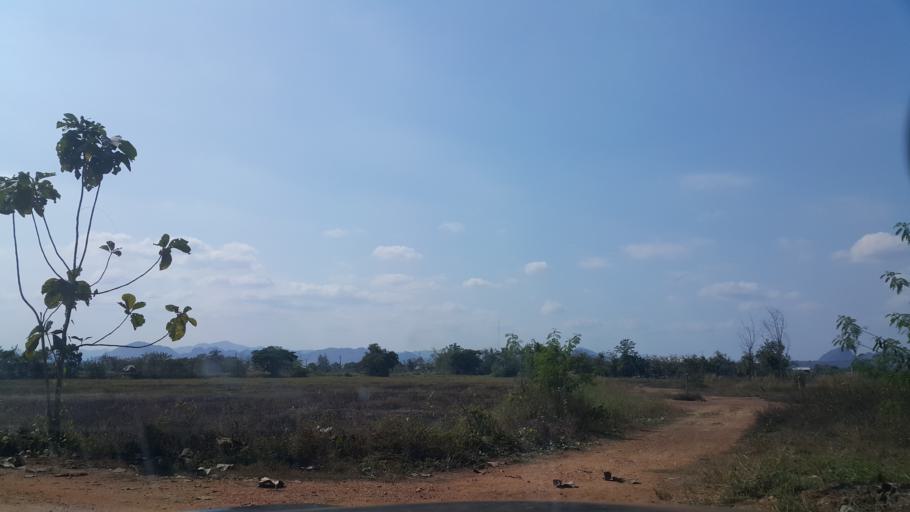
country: TH
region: Sukhothai
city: Thung Saliam
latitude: 17.3282
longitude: 99.5768
